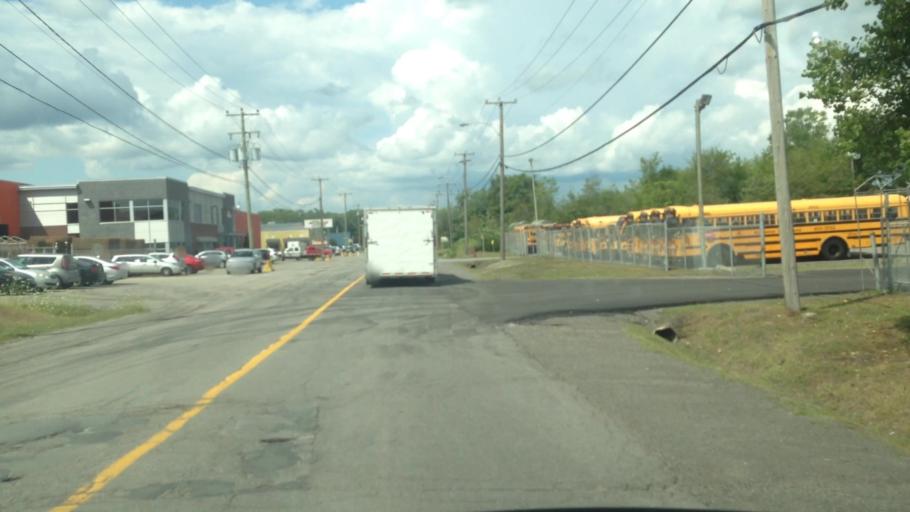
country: CA
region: Quebec
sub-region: Laurentides
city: Saint-Jerome
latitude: 45.7656
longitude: -74.0228
